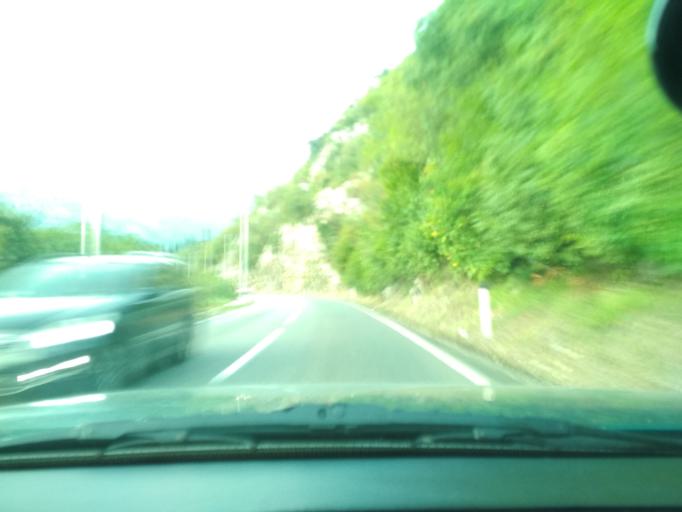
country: ME
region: Kotor
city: Risan
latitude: 42.4974
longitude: 18.6918
